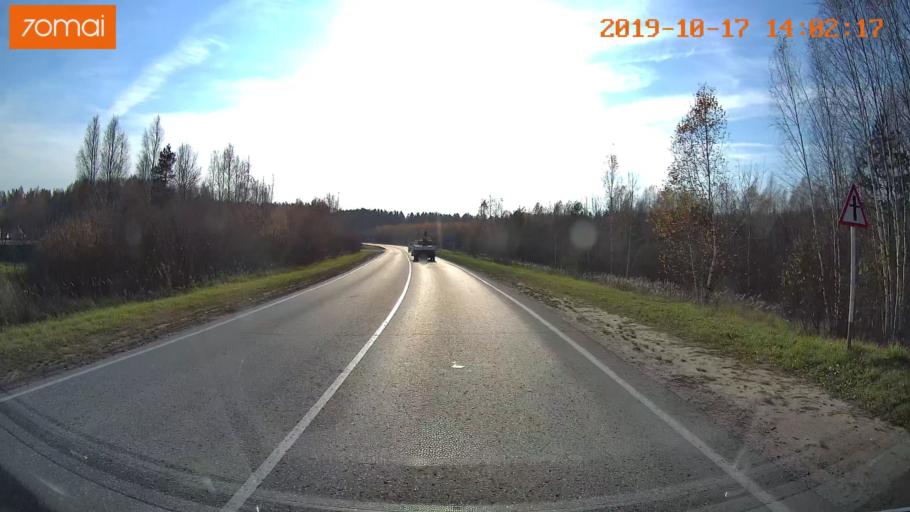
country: RU
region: Rjazan
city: Spas-Klepiki
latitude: 55.1482
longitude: 40.1522
